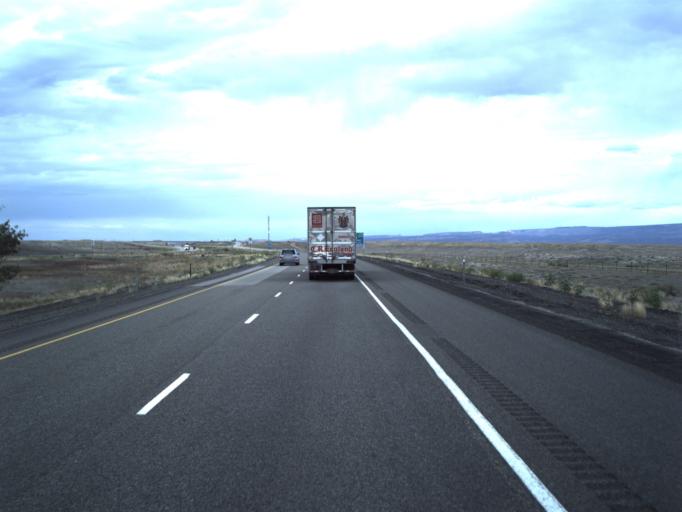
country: US
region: Utah
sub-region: Grand County
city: Moab
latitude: 38.9331
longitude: -109.4223
